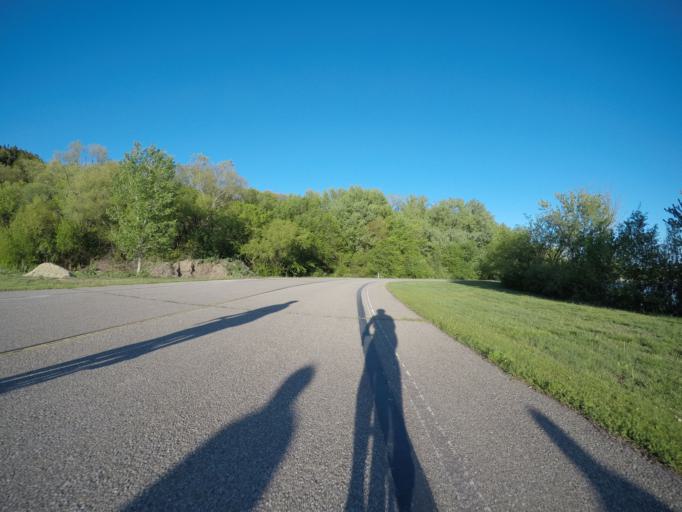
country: US
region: Kansas
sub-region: Riley County
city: Manhattan
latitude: 39.2556
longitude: -96.5772
